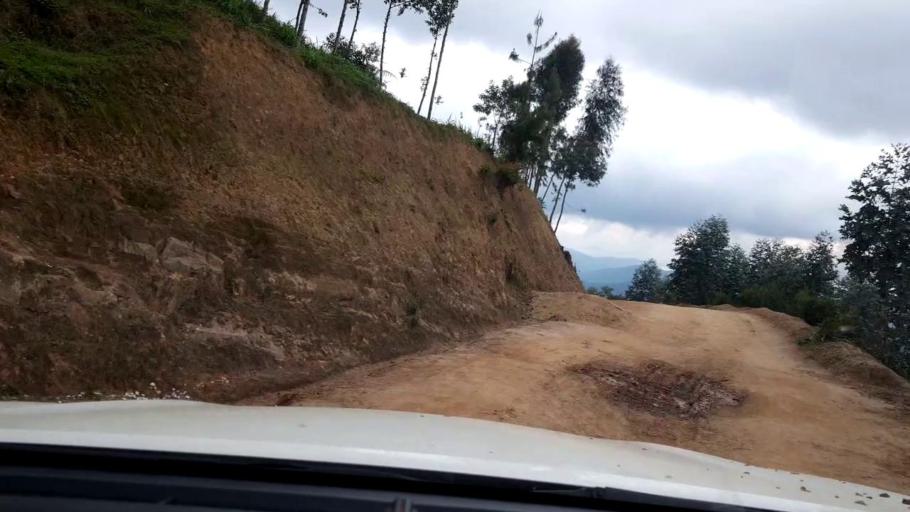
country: RW
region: Western Province
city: Kibuye
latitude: -1.8951
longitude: 29.5273
